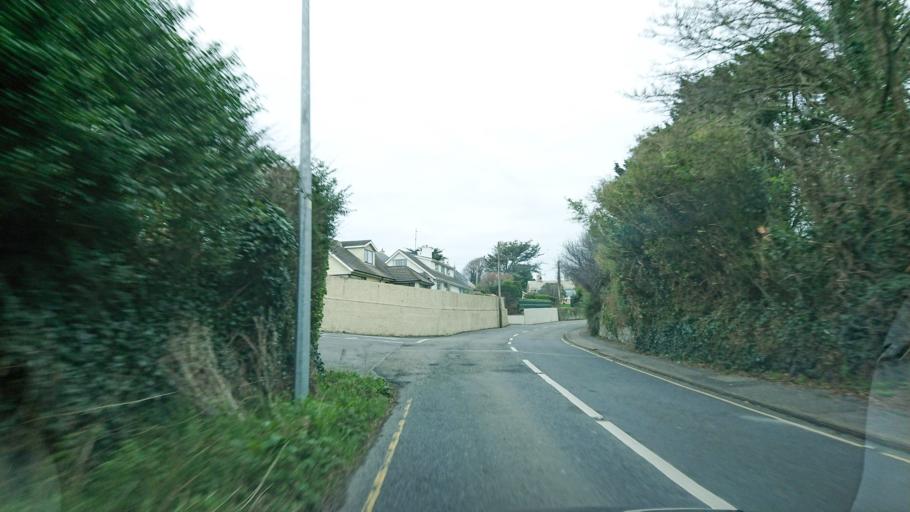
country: IE
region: Munster
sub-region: Waterford
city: Tra Mhor
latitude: 52.1543
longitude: -7.1614
